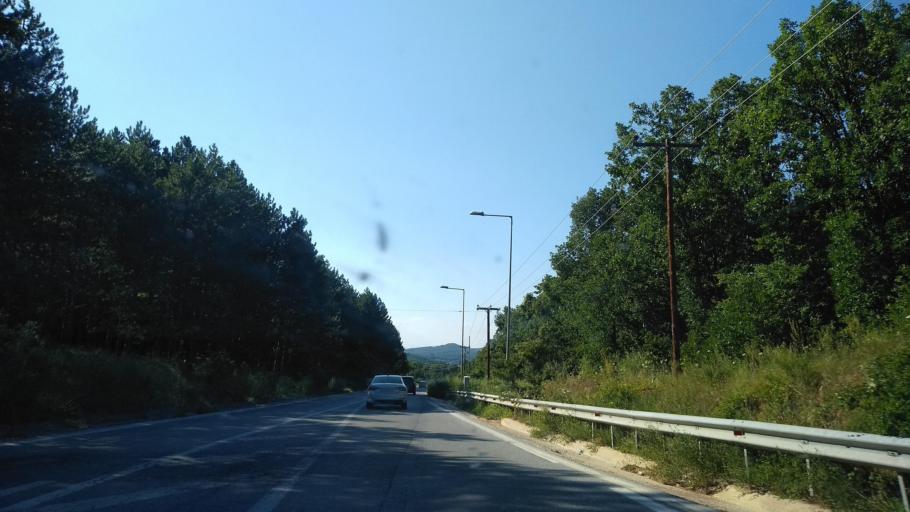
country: GR
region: Central Macedonia
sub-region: Nomos Chalkidikis
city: Megali Panagia
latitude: 40.4582
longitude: 23.6566
